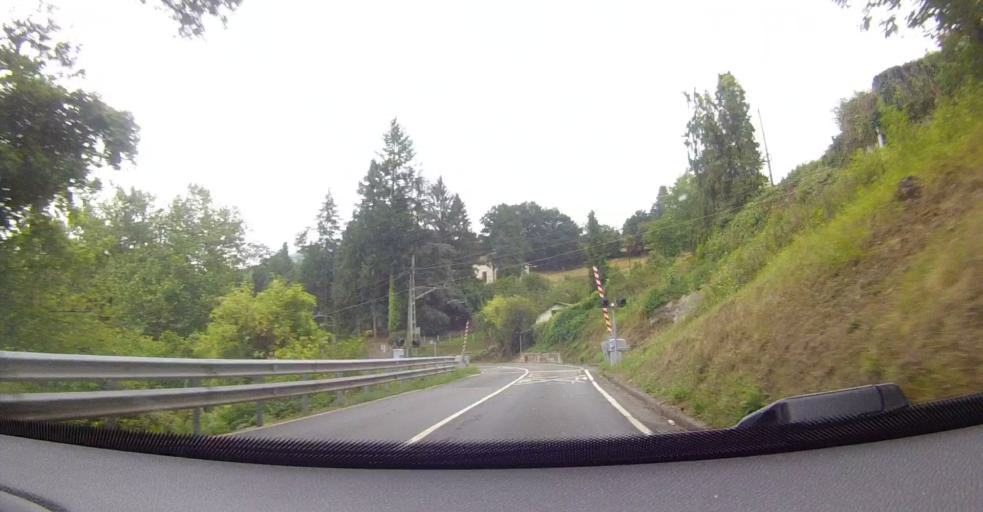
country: ES
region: Basque Country
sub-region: Bizkaia
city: Balmaseda
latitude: 43.2358
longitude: -3.2061
